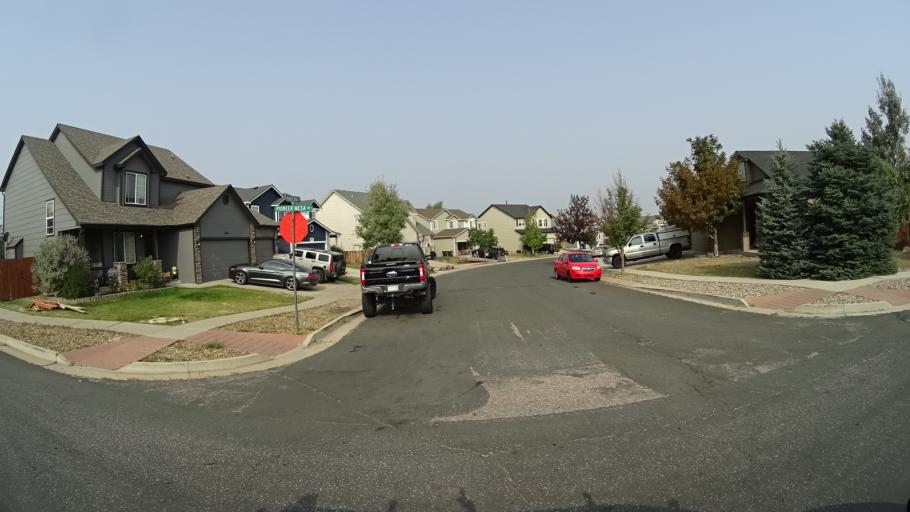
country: US
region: Colorado
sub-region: El Paso County
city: Cimarron Hills
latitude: 38.9324
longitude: -104.7328
